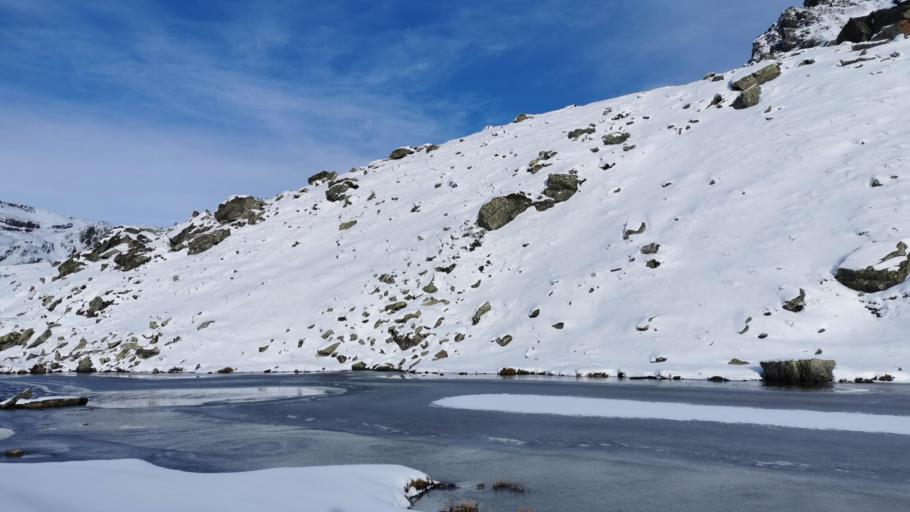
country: FR
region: Provence-Alpes-Cote d'Azur
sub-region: Departement des Hautes-Alpes
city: Le Monetier-les-Bains
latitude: 45.0784
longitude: 6.5205
